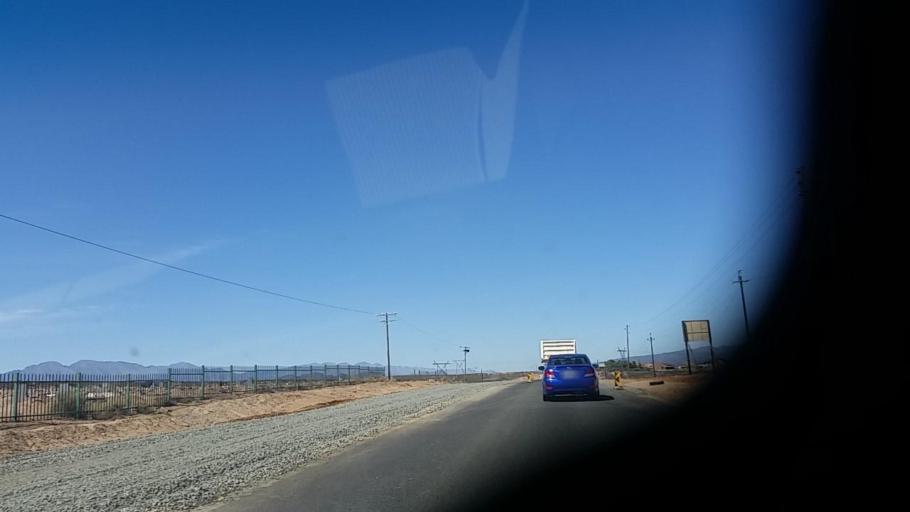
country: ZA
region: Western Cape
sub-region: Eden District Municipality
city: Oudtshoorn
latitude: -33.5924
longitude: 22.2348
